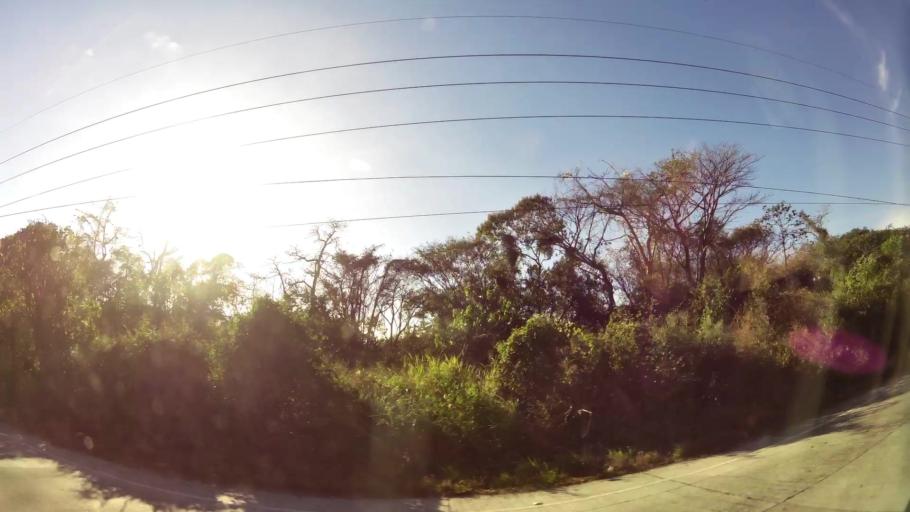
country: SV
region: Santa Ana
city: Metapan
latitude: 14.2690
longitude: -89.4606
